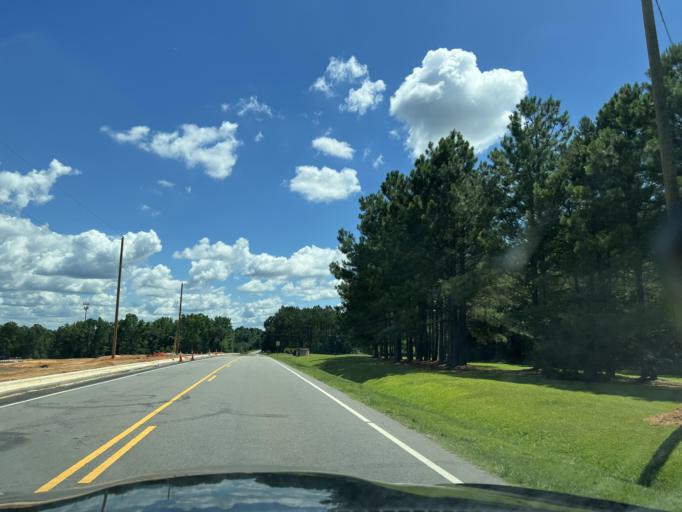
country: US
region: North Carolina
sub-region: Lee County
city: Sanford
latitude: 35.4523
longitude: -79.1700
